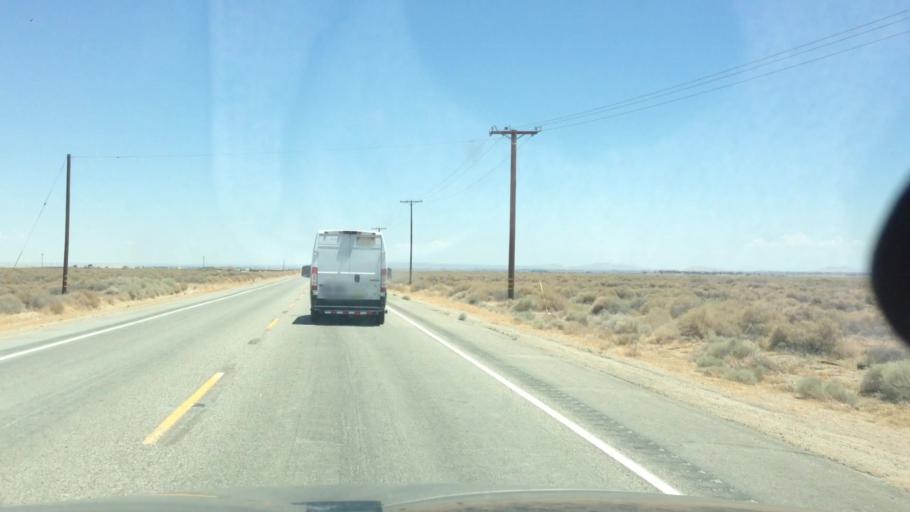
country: US
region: California
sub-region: Kern County
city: Rosamond
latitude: 34.7765
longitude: -118.2201
